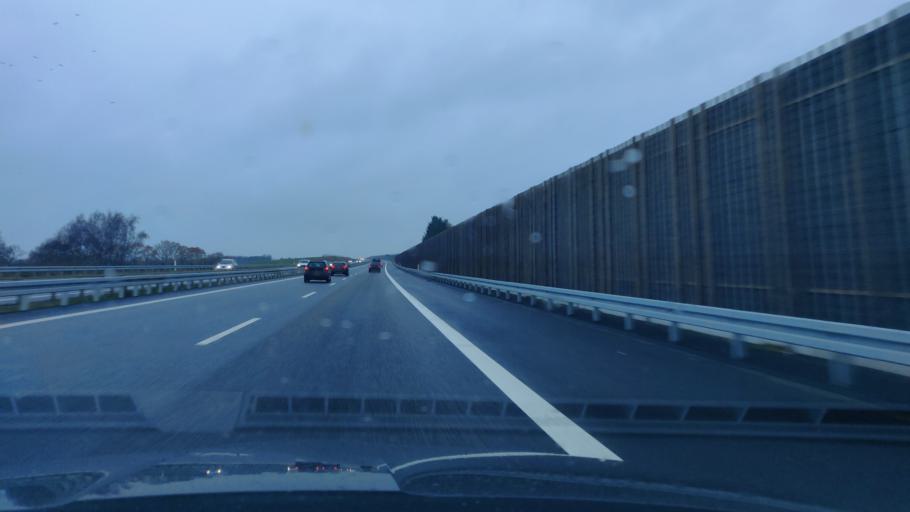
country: DK
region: Central Jutland
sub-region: Herning Kommune
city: Avlum
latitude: 56.2376
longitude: 8.8065
